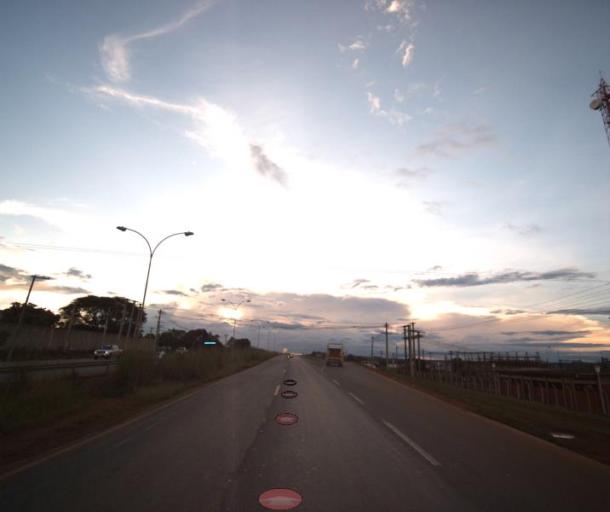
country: BR
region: Goias
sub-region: Anapolis
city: Anapolis
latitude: -16.2873
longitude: -48.9417
